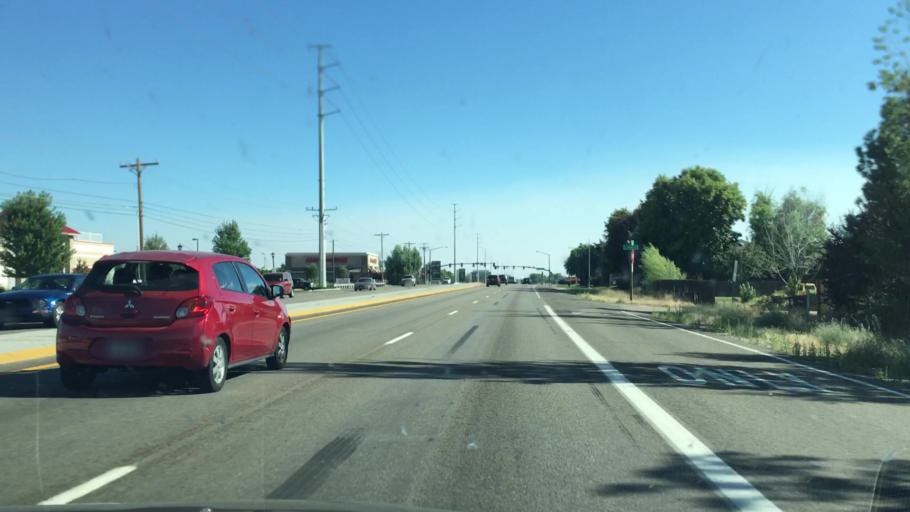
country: US
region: Idaho
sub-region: Ada County
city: Meridian
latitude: 43.6292
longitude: -116.3546
